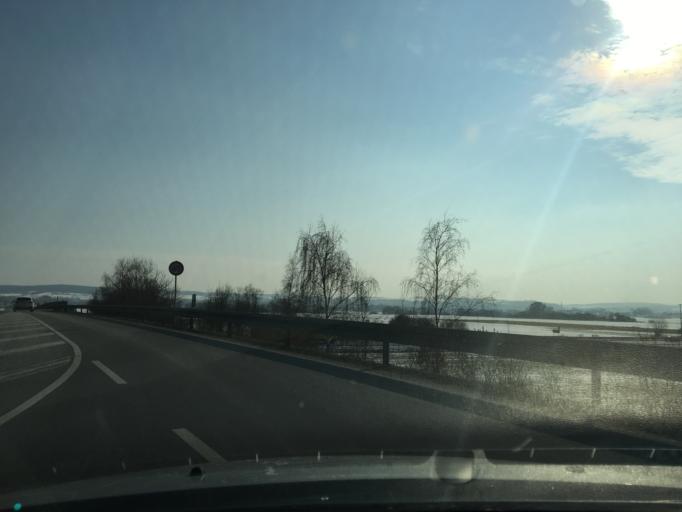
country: DE
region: Bavaria
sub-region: Lower Bavaria
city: Gottfrieding
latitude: 48.6634
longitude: 12.5227
